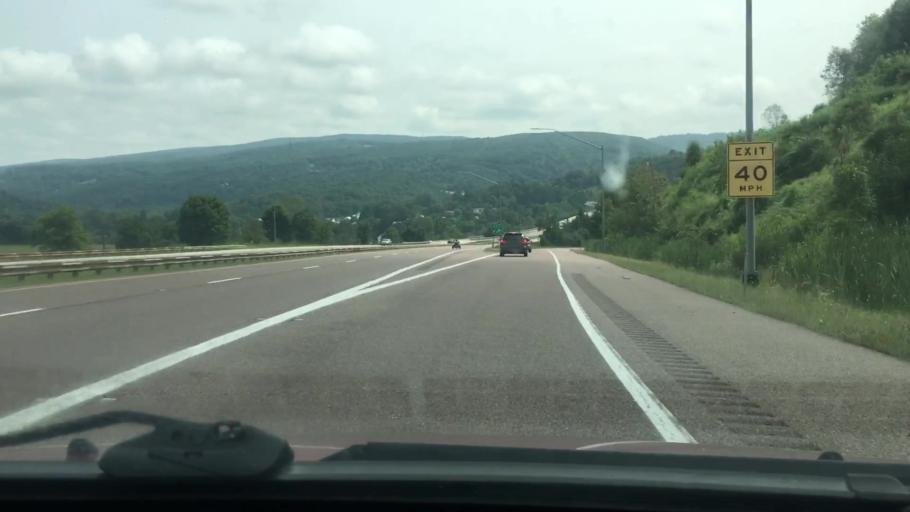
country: US
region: West Virginia
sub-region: Preston County
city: Terra Alta
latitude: 39.6620
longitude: -79.4167
